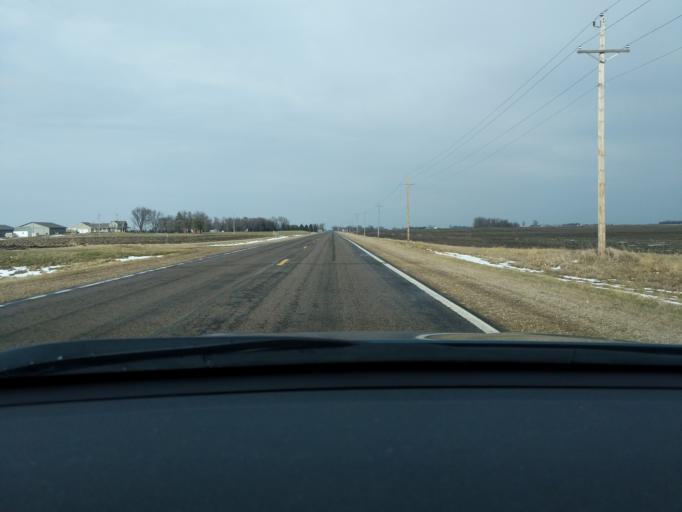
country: US
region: Minnesota
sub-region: Renville County
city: Renville
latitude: 44.7632
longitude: -95.3409
